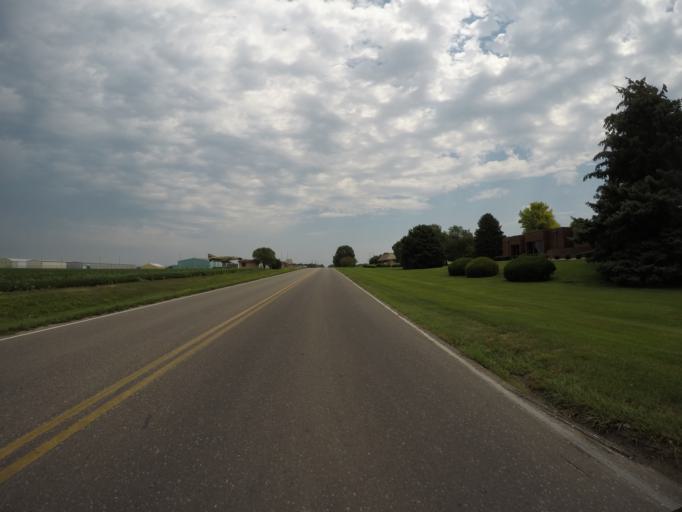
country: US
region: Nebraska
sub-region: Adams County
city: Hastings
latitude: 40.5970
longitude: -98.4291
